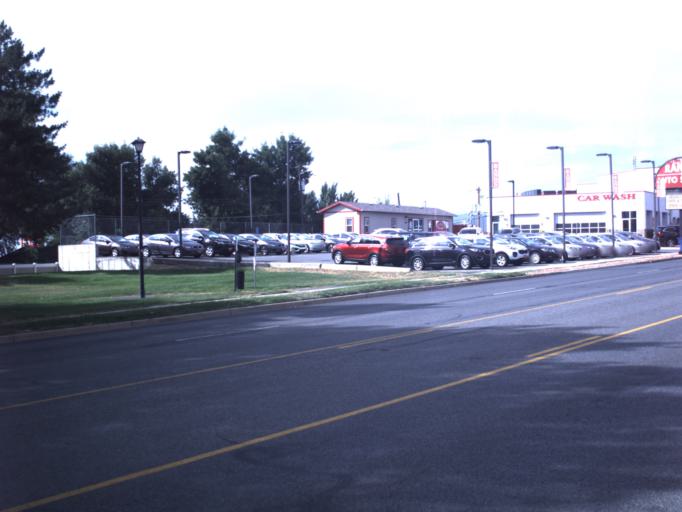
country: US
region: Utah
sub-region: Davis County
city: North Salt Lake
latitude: 40.8582
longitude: -111.8990
